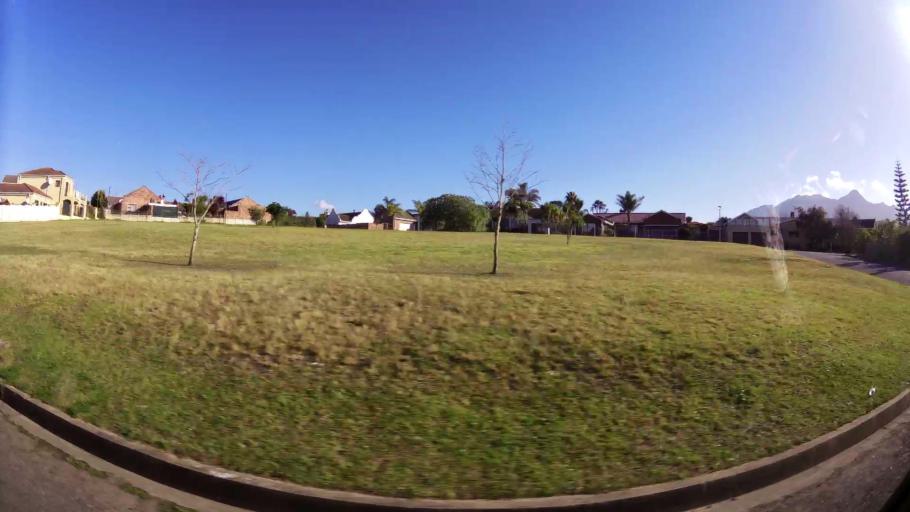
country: ZA
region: Western Cape
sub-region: Eden District Municipality
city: George
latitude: -33.9711
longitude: 22.4406
